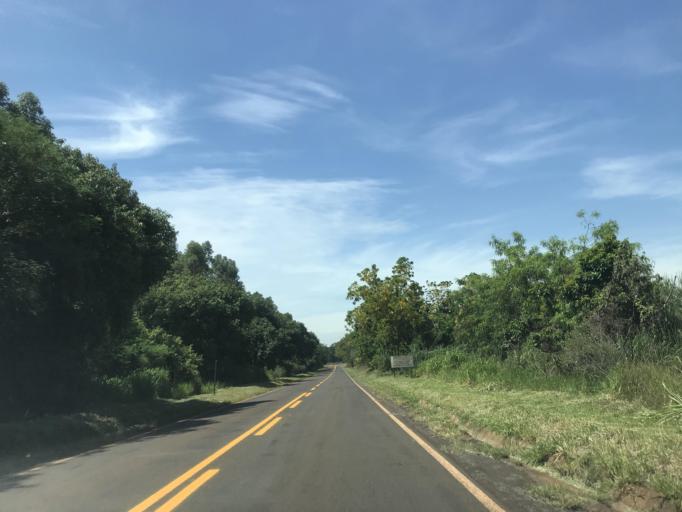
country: BR
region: Parana
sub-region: Terra Rica
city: Terra Rica
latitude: -22.7896
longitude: -52.6547
